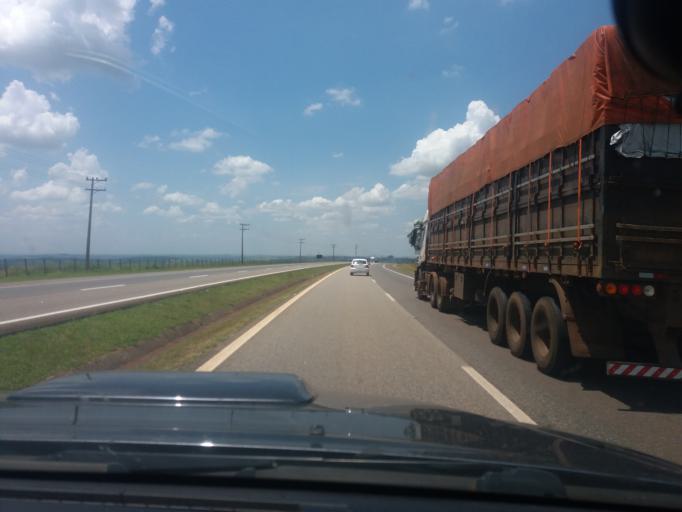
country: BR
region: Sao Paulo
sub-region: Itapetininga
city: Itapetininga
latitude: -23.5347
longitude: -47.9641
